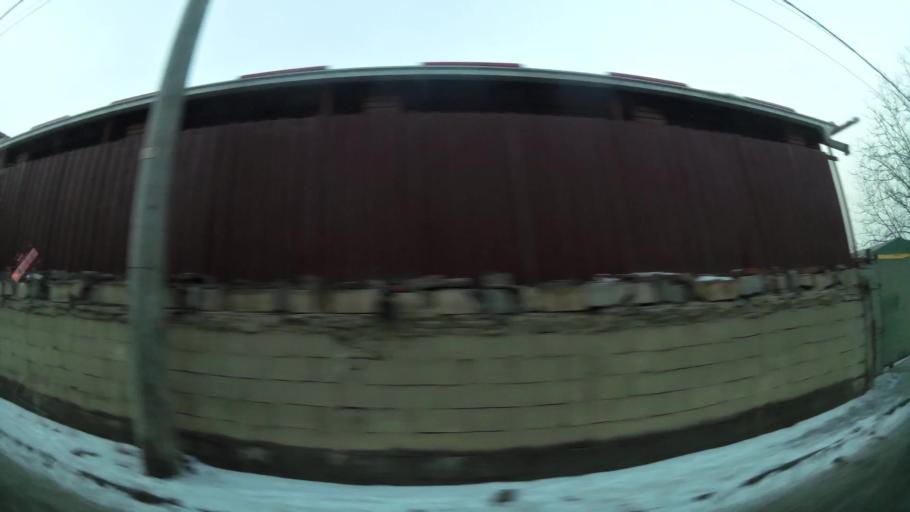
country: MK
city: Creshevo
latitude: 42.0031
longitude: 21.5055
